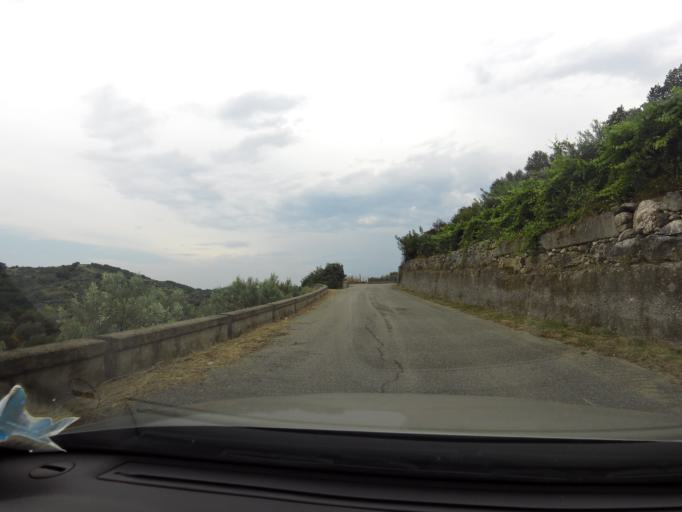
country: IT
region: Calabria
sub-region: Provincia di Reggio Calabria
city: Pazzano
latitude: 38.4590
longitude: 16.4499
